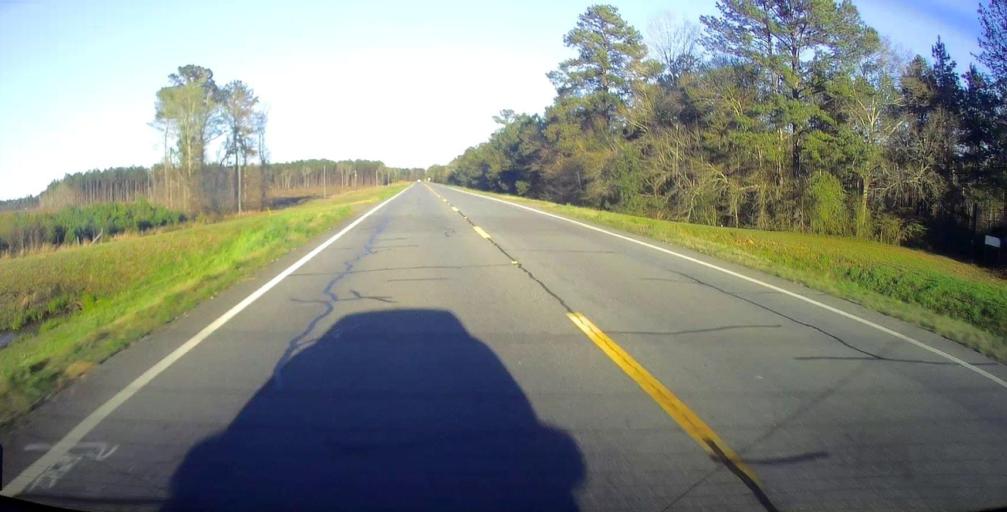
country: US
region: Georgia
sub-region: Wilcox County
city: Abbeville
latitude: 31.9995
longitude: -83.2618
